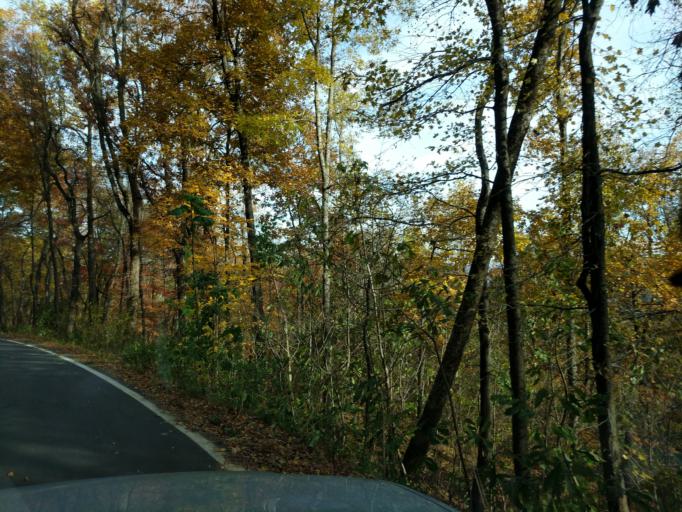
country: US
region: North Carolina
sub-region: Polk County
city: Columbus
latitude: 35.2620
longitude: -82.2362
